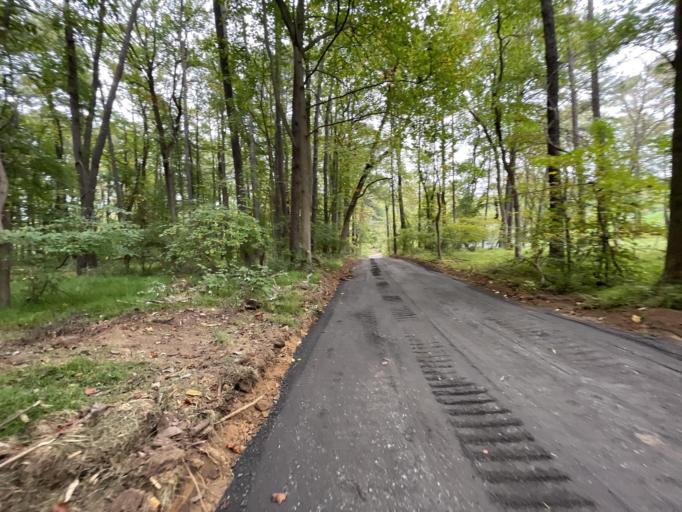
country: US
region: Maryland
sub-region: Baltimore County
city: Hampton
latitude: 39.4284
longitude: -76.5822
